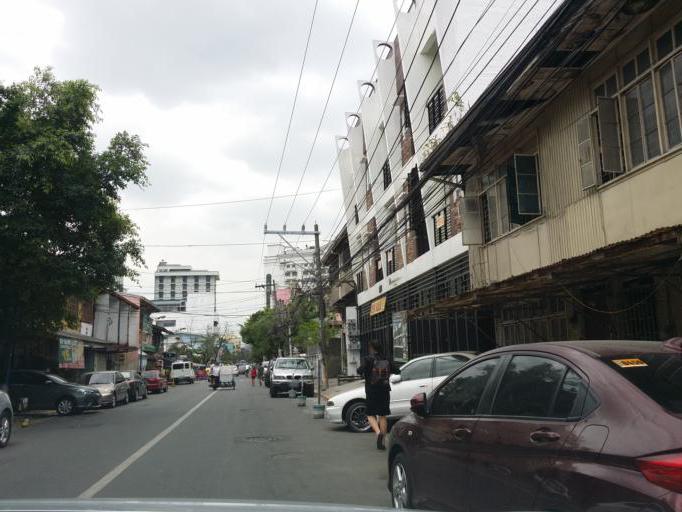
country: PH
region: Metro Manila
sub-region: Makati City
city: Makati City
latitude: 14.5670
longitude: 121.0002
